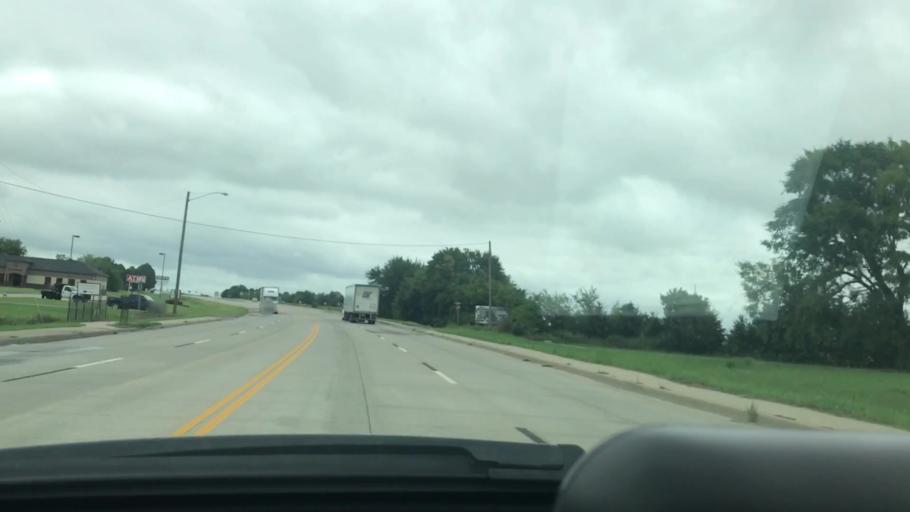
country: US
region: Oklahoma
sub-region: Pittsburg County
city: McAlester
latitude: 34.7260
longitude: -95.8983
